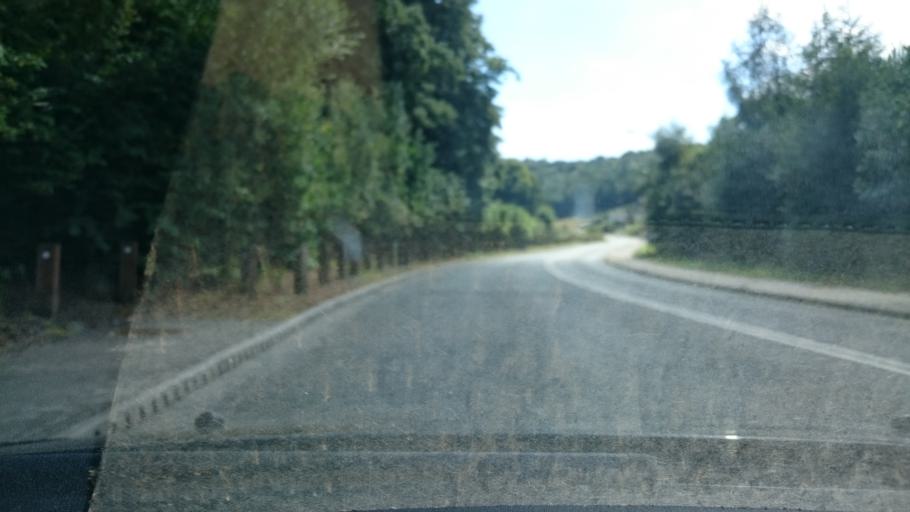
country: IE
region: Leinster
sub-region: Kilkenny
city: Graiguenamanagh
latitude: 52.5374
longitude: -6.9631
